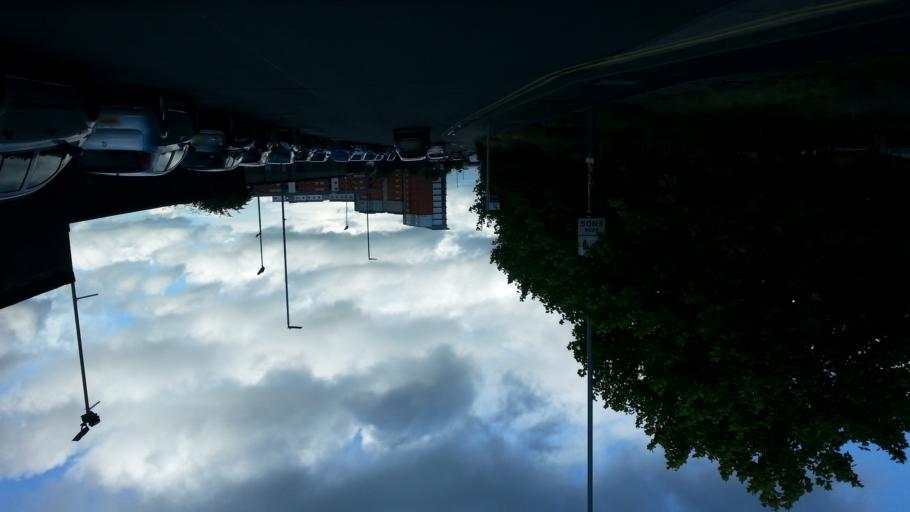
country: GB
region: England
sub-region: City and Borough of Birmingham
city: Birmingham
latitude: 52.4821
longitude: -1.8855
